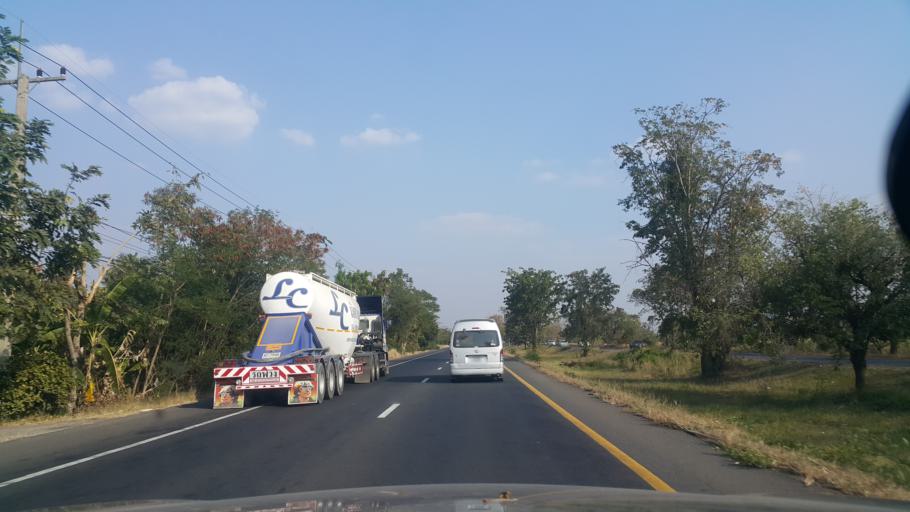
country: TH
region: Buriram
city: Non Suwan
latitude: 14.6584
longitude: 102.6310
